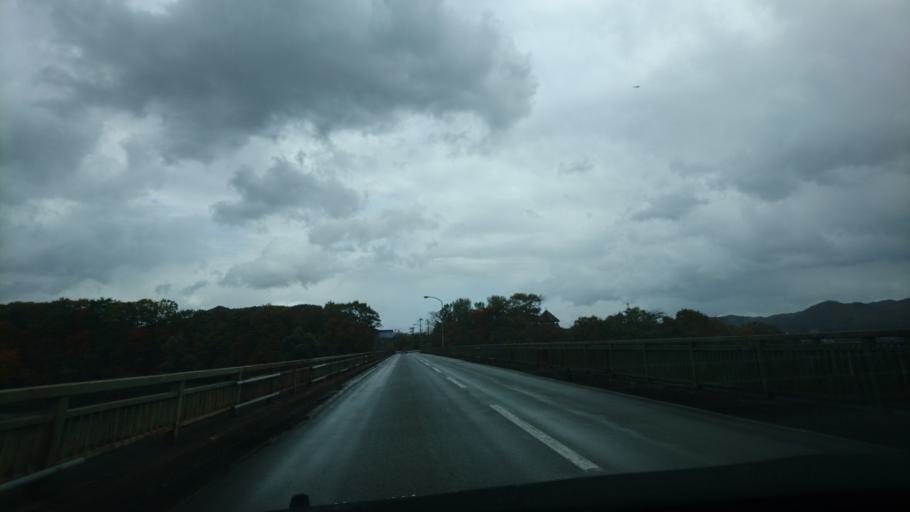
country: JP
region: Iwate
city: Shizukuishi
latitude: 39.6748
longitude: 140.9901
